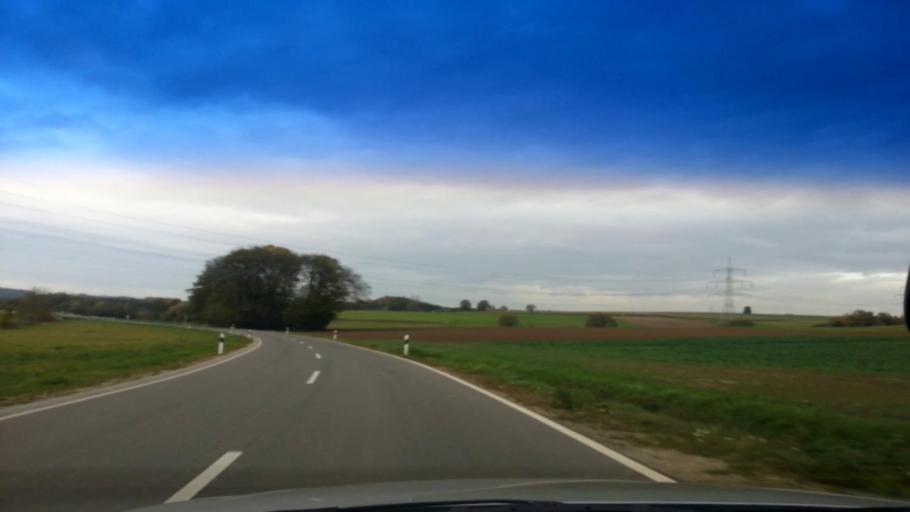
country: DE
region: Bavaria
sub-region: Upper Franconia
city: Memmelsdorf
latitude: 49.9506
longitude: 10.9684
